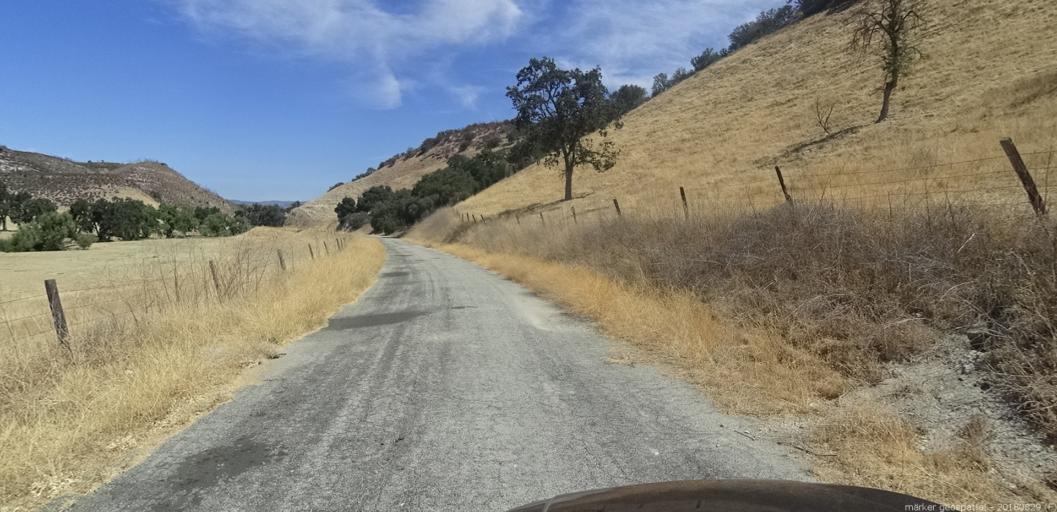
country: US
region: California
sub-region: San Luis Obispo County
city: Lake Nacimiento
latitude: 35.8394
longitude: -121.0365
